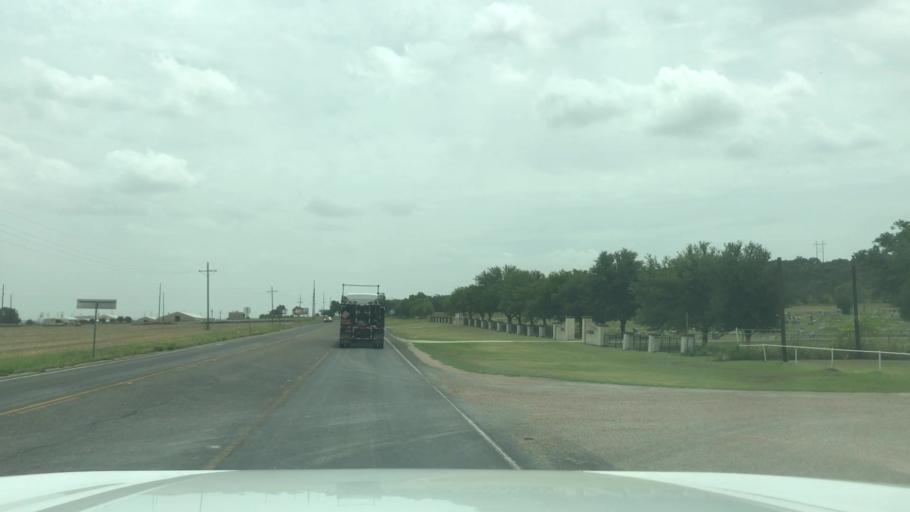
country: US
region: Texas
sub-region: Bosque County
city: Clifton
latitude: 31.7739
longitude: -97.5722
